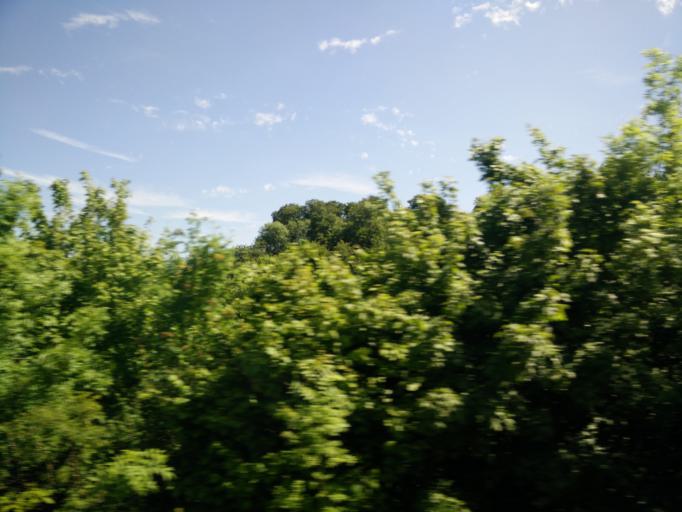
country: GB
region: England
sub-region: Hertfordshire
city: Hemel Hempstead
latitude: 51.7371
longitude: -0.4778
